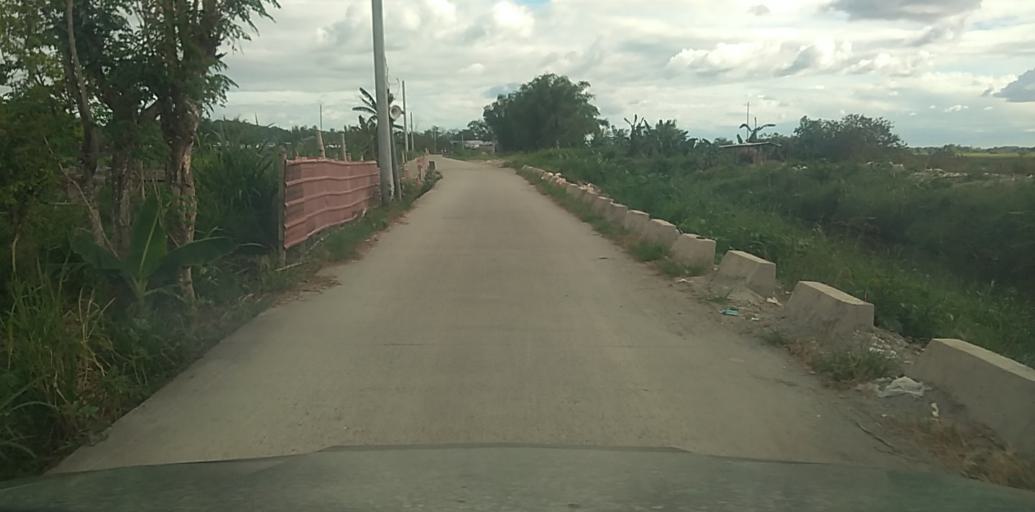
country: PH
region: Central Luzon
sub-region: Province of Pampanga
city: Panlinlang
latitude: 15.1788
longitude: 120.7010
